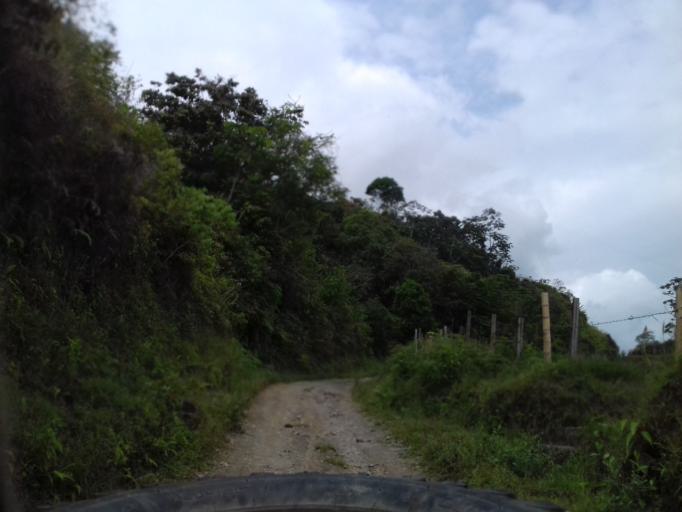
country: CO
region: Tolima
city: Libano
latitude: 4.9293
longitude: -75.0897
